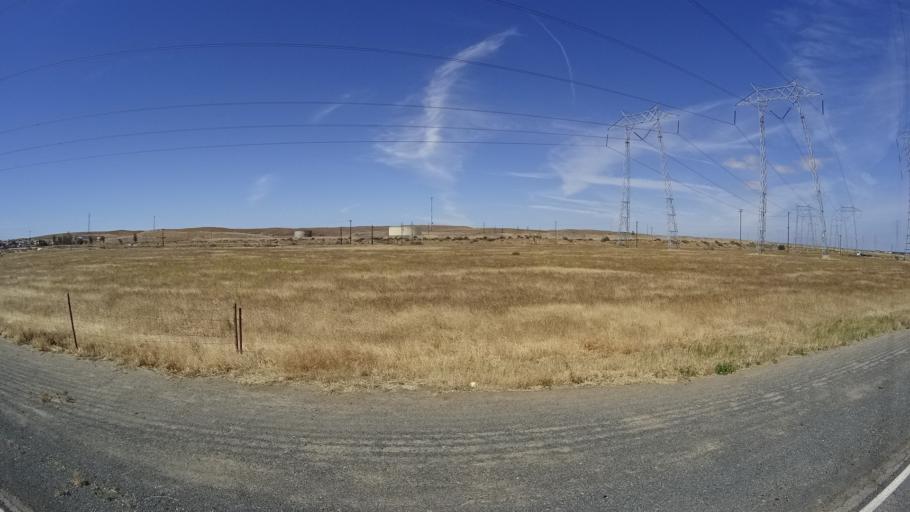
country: US
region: California
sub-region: Kings County
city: Kettleman City
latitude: 35.9971
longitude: -119.9572
